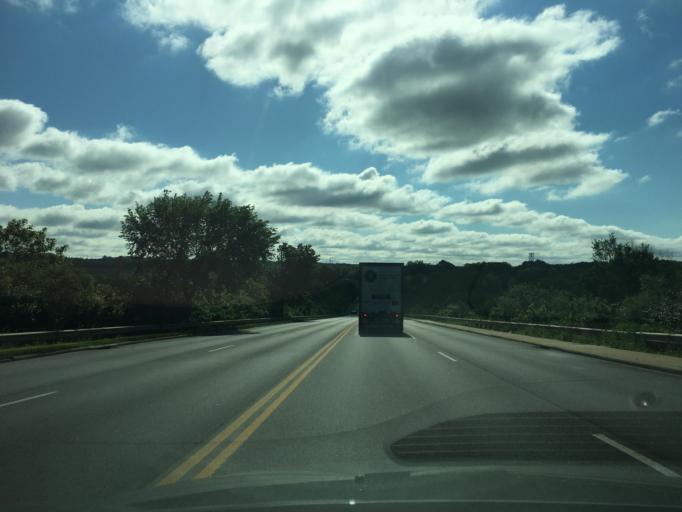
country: US
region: Ohio
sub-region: Cuyahoga County
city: Independence
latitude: 41.3942
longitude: -81.6370
